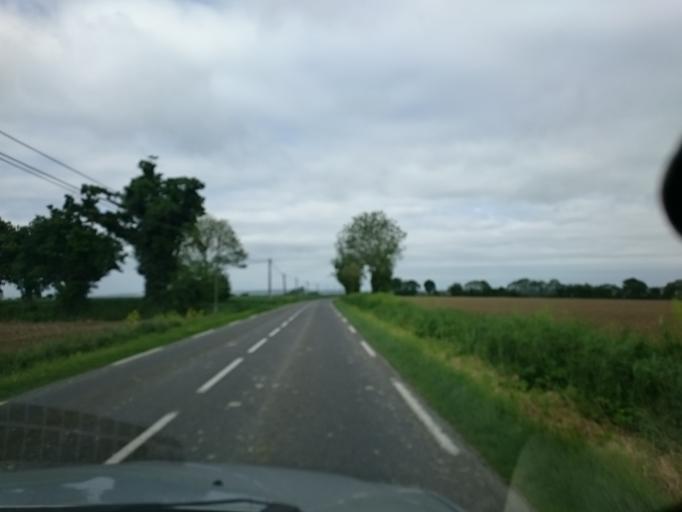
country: FR
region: Lower Normandy
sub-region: Departement de la Manche
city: Pontorson
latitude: 48.5552
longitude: -1.4441
